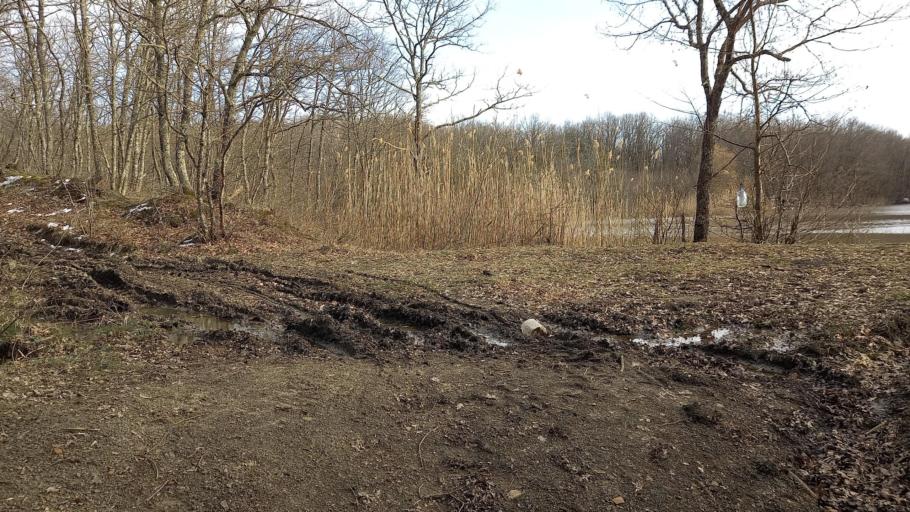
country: RU
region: Krasnodarskiy
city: Smolenskaya
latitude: 44.5957
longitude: 38.8463
